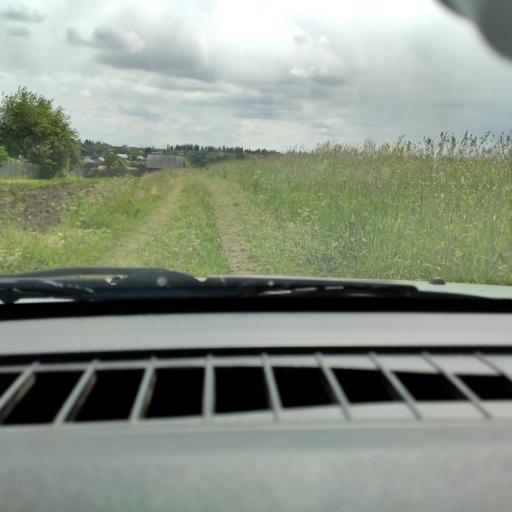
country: RU
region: Perm
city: Uinskoye
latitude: 57.1147
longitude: 56.5028
